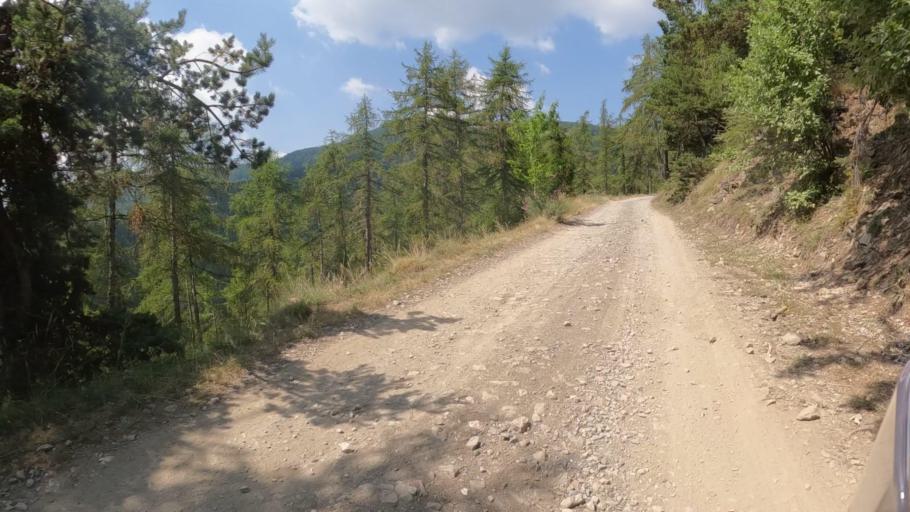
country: IT
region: Piedmont
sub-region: Provincia di Cuneo
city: Briga Alta
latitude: 44.0295
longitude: 7.6754
